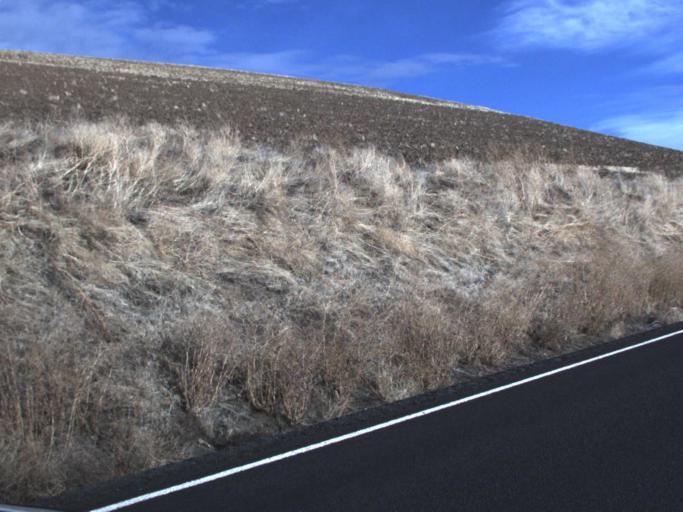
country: US
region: Washington
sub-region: Whitman County
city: Colfax
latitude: 46.8903
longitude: -117.3367
